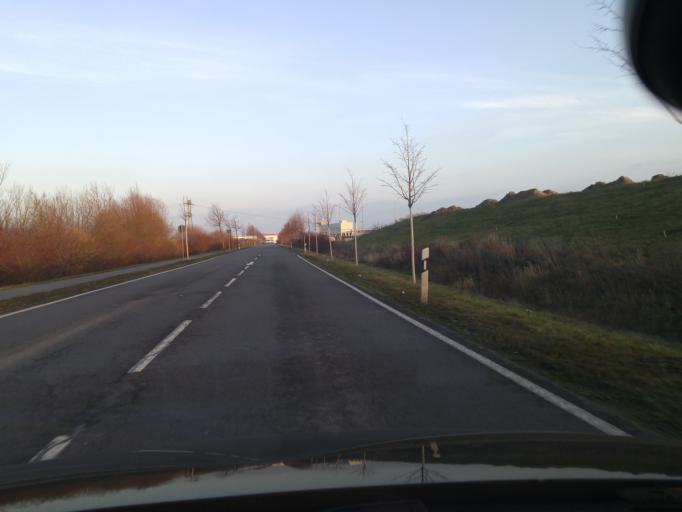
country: DE
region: Saxony
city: Zwochau
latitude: 51.4143
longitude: 12.2807
